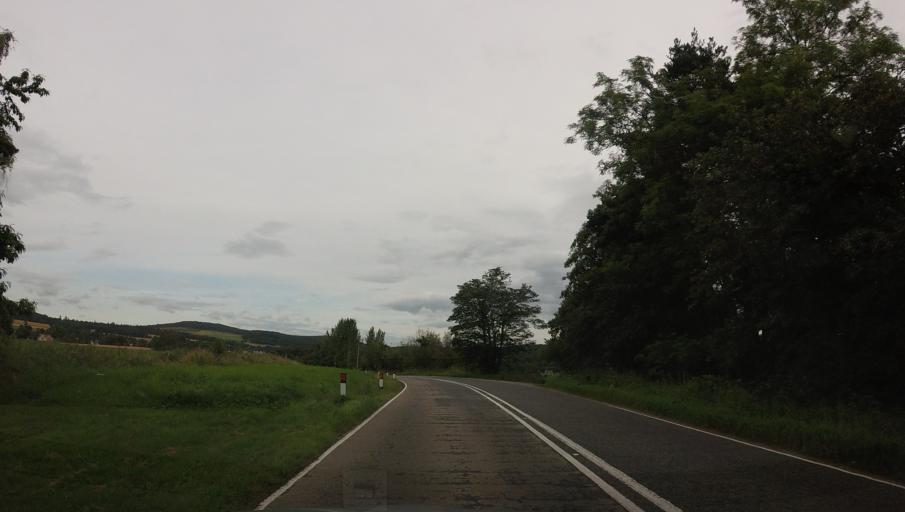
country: GB
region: Scotland
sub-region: Aberdeenshire
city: Torphins
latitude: 57.0881
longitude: -2.6889
